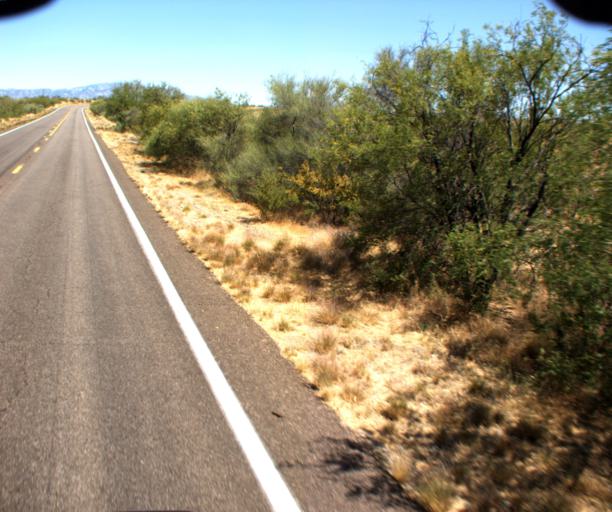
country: US
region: Arizona
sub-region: Pima County
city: Catalina
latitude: 32.6192
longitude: -110.9921
